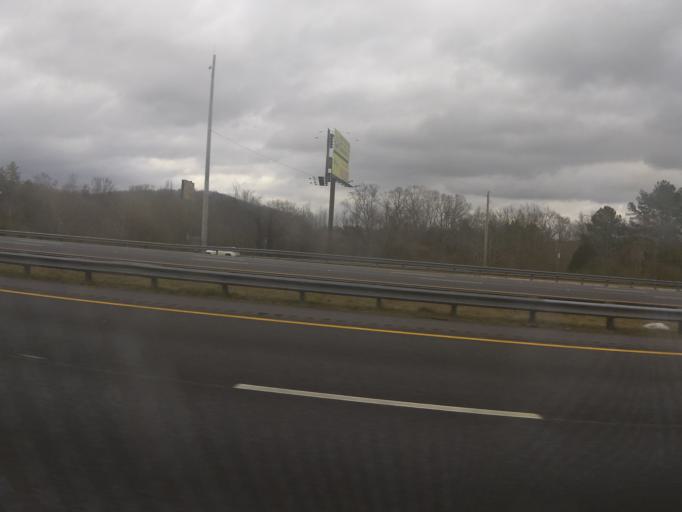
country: US
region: Georgia
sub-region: Whitfield County
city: Varnell
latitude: 34.8590
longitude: -85.0229
